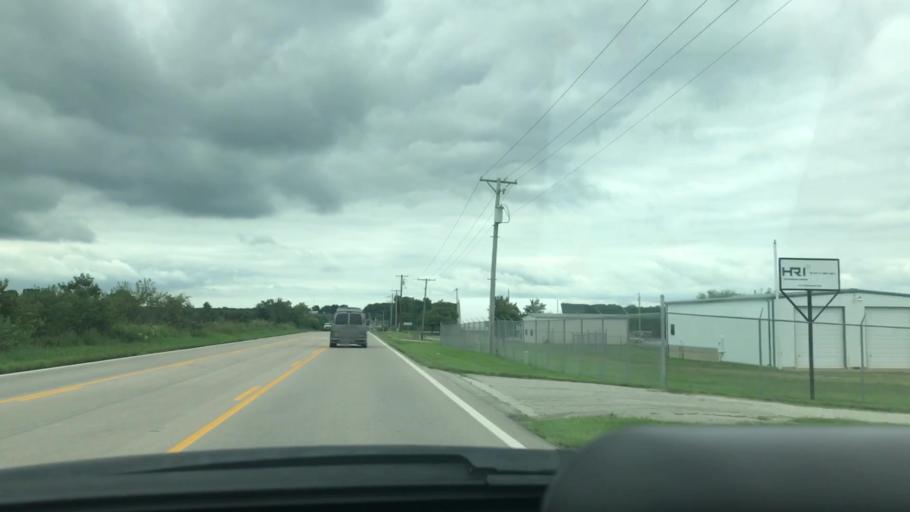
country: US
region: Missouri
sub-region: Dallas County
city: Buffalo
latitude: 37.6586
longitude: -93.1036
